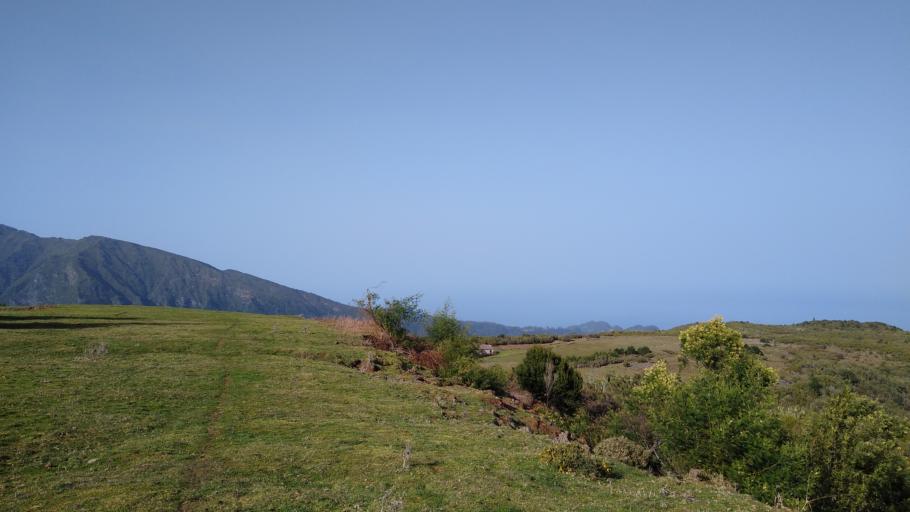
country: PT
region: Madeira
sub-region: Funchal
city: Nossa Senhora do Monte
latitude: 32.7251
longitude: -16.8860
